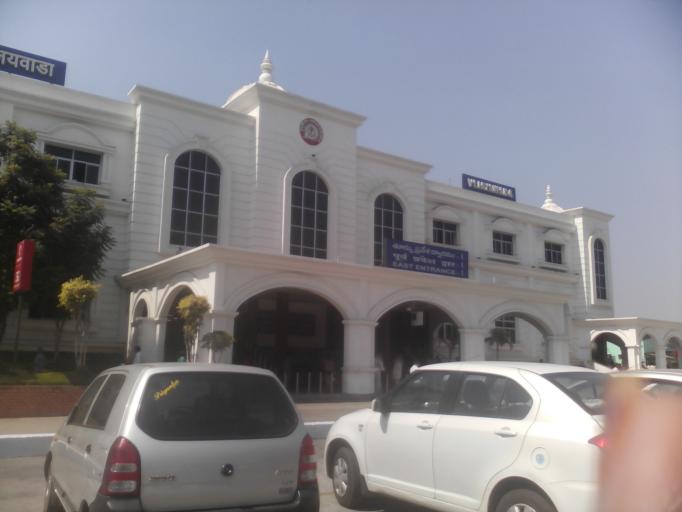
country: IN
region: Andhra Pradesh
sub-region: Krishna
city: Vijayawada
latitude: 16.5162
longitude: 80.6190
